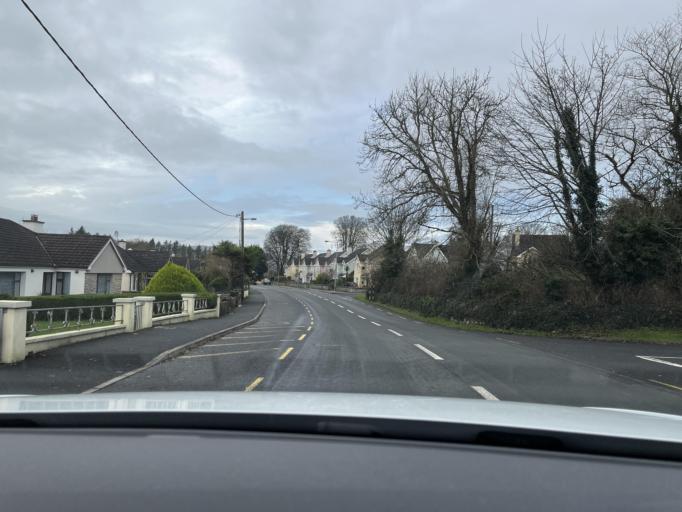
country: IE
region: Connaught
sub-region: County Leitrim
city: Manorhamilton
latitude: 54.2290
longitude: -8.2955
